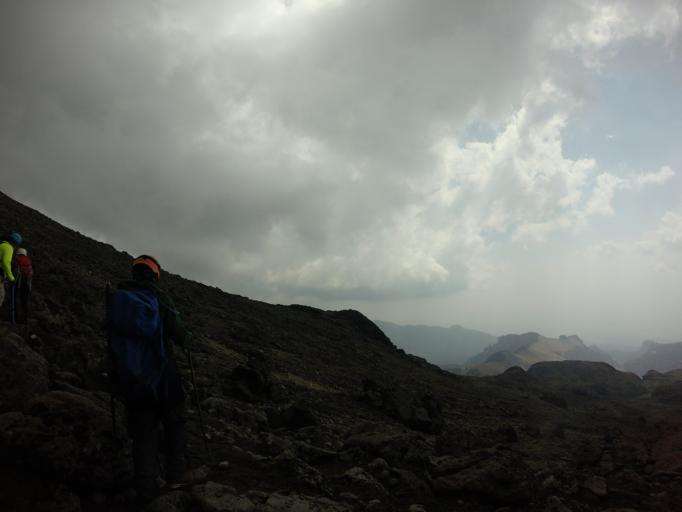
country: MX
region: Mexico
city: Amecameca de Juarez
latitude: 19.1542
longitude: -98.6414
